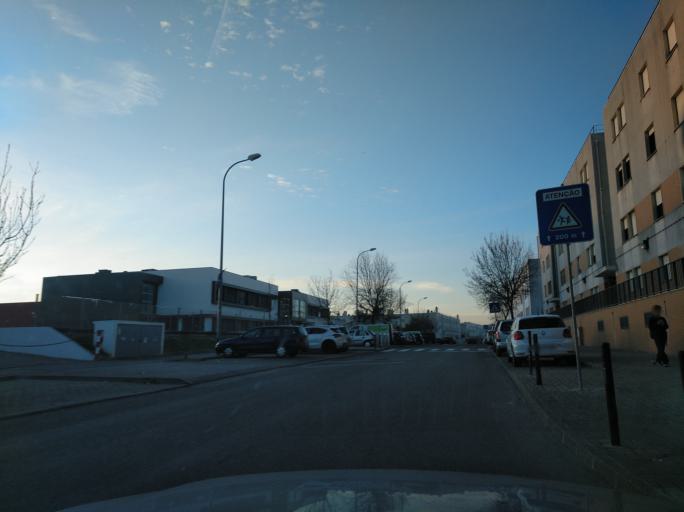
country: PT
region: Lisbon
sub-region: Odivelas
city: Olival do Basto
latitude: 38.7905
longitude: -9.1509
